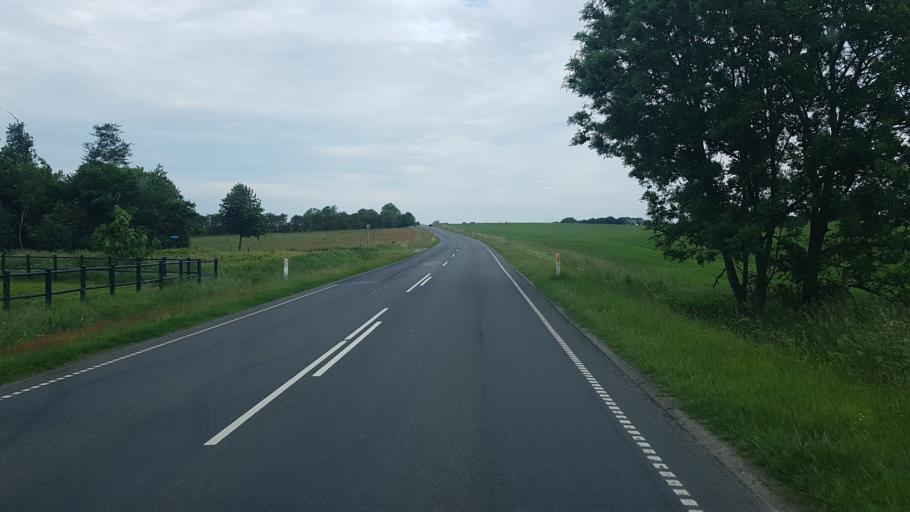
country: DK
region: South Denmark
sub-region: Vejen Kommune
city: Rodding
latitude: 55.3947
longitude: 9.0392
